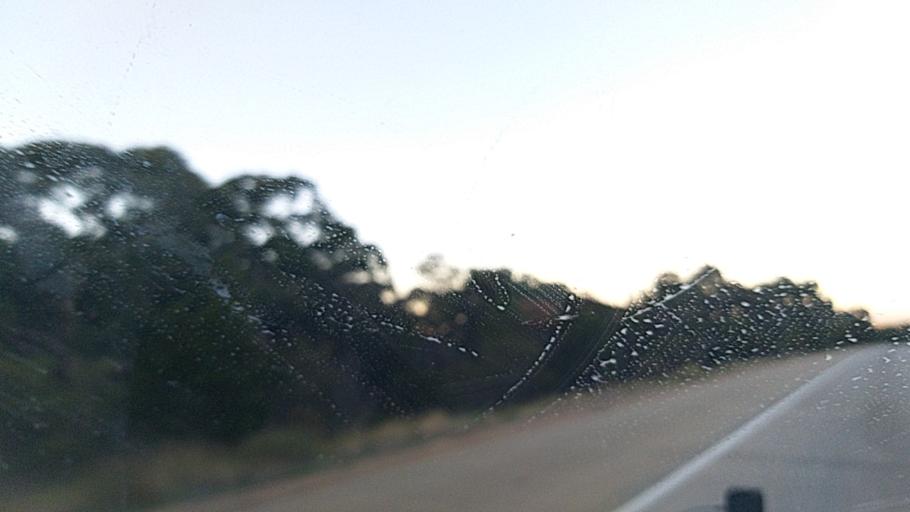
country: AU
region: New South Wales
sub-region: Goulburn Mulwaree
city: Goulburn
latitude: -34.7644
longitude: 149.7645
